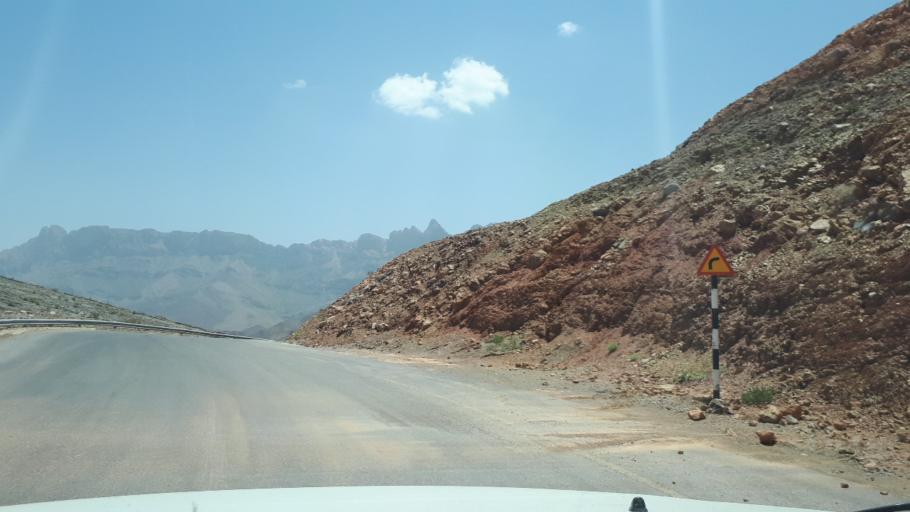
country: OM
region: Muhafazat ad Dakhiliyah
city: Bahla'
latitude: 23.1977
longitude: 57.1382
